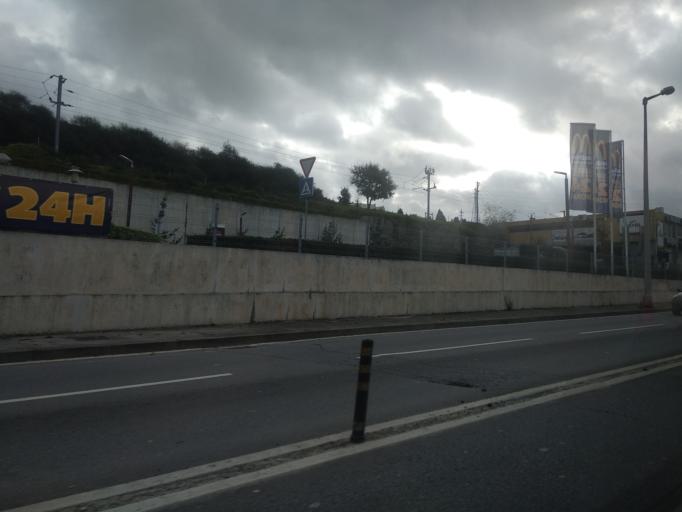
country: PT
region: Braga
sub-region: Guimaraes
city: Urgeses
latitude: 41.4317
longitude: -8.3020
